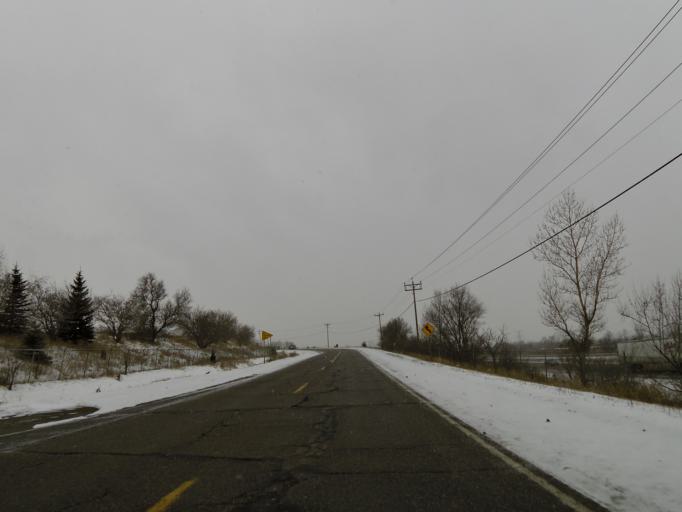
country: US
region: Minnesota
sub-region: Washington County
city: Lakeland
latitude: 44.9520
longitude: -92.8039
